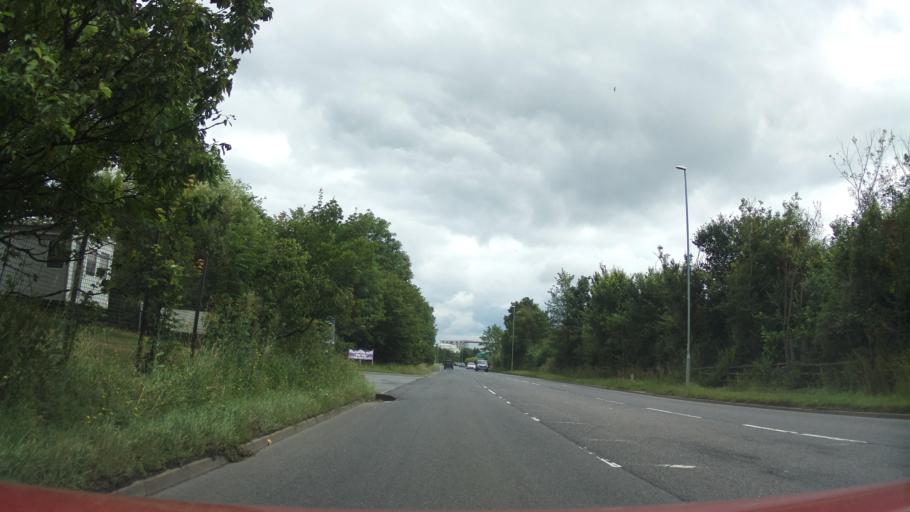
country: GB
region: England
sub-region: Northamptonshire
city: Corby
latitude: 52.5114
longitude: -0.6940
